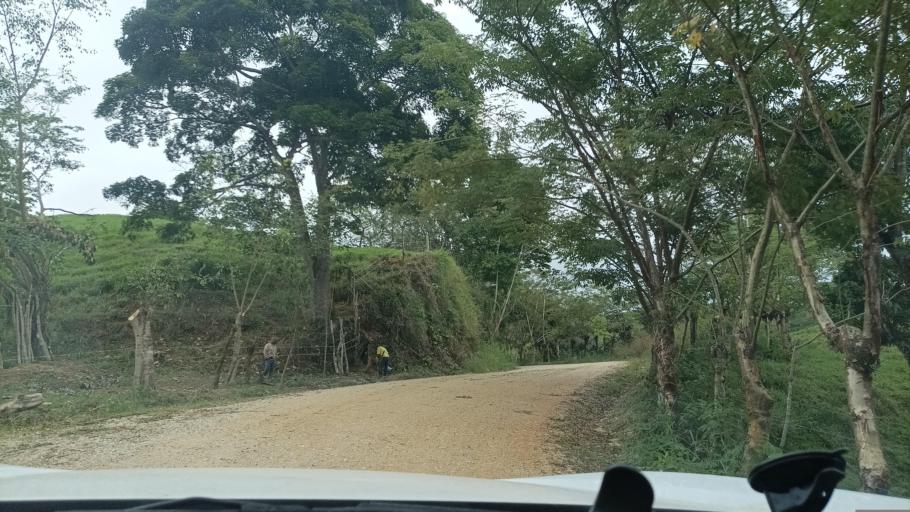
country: MX
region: Veracruz
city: Hidalgotitlan
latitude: 17.6175
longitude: -94.5161
